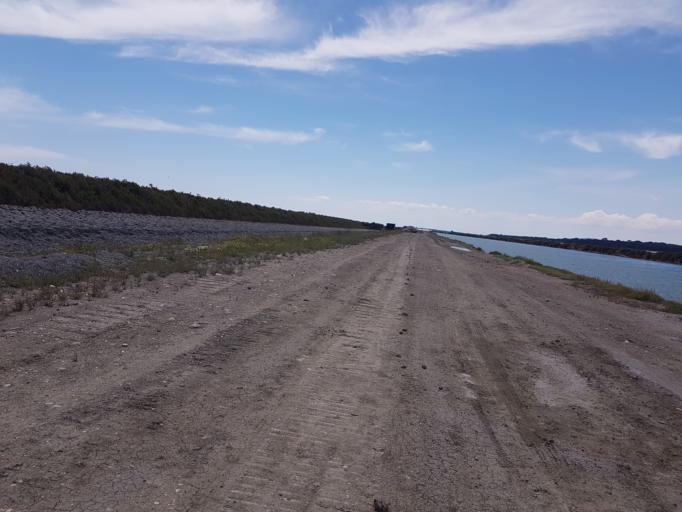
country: FR
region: Languedoc-Roussillon
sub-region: Departement de l'Herault
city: Vic-la-Gardiole
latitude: 43.4762
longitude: 3.8306
